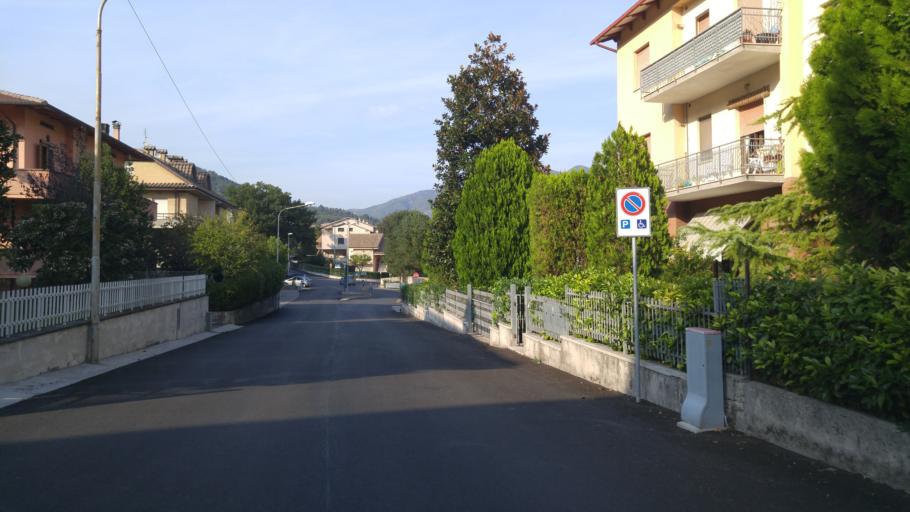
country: IT
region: The Marches
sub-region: Provincia di Pesaro e Urbino
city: Acqualagna
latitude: 43.6202
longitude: 12.6725
